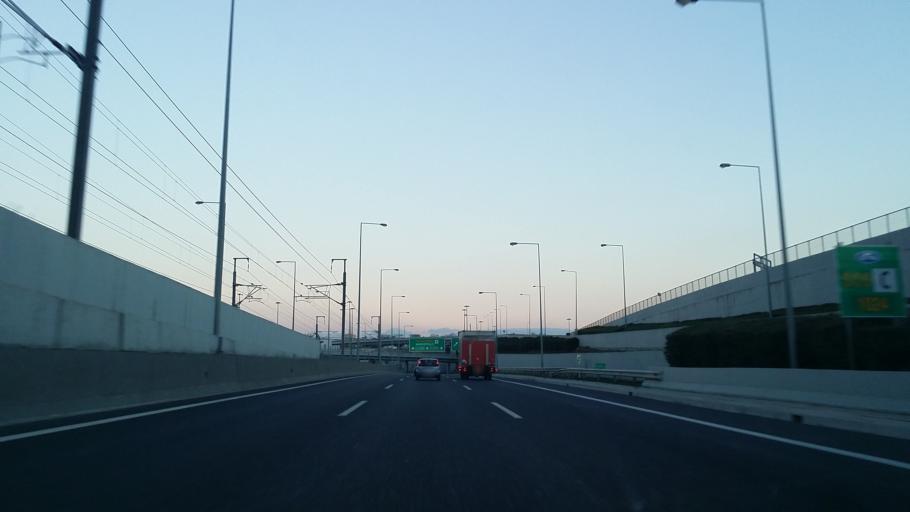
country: GR
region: Attica
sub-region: Nomarchia Athinas
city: Metamorfosi
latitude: 38.0639
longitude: 23.7434
